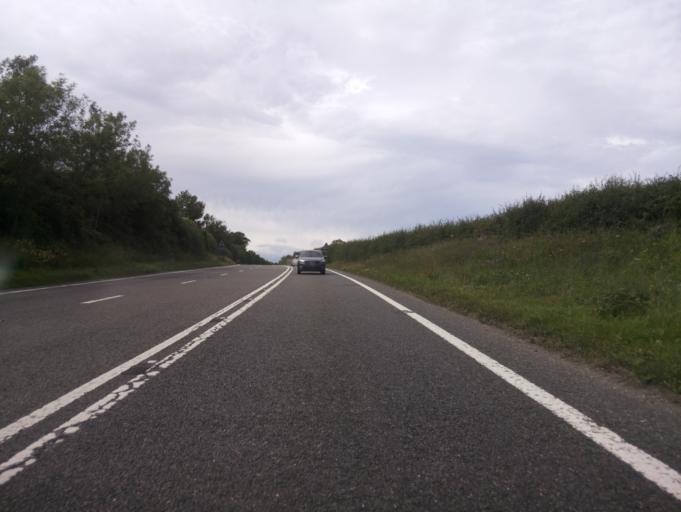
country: GB
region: England
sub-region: Somerset
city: Yeovil
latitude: 50.8428
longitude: -2.5805
